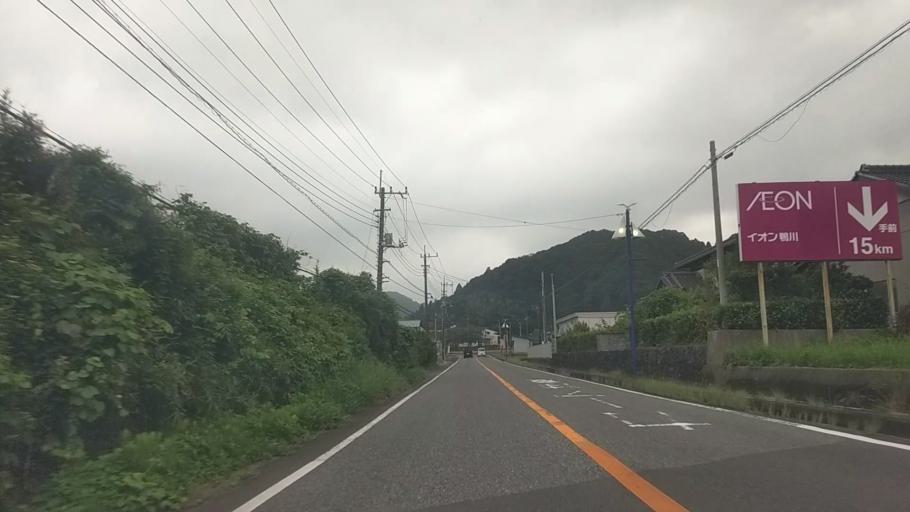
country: JP
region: Chiba
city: Kawaguchi
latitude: 35.1432
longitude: 139.9717
